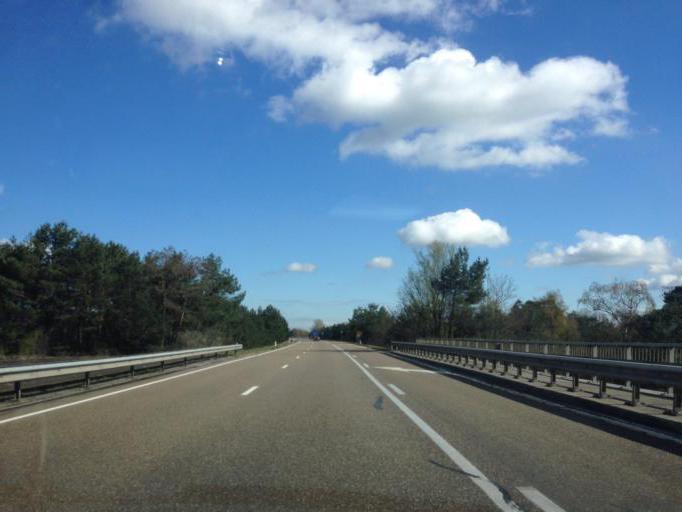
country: BE
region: Flanders
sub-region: Provincie Limburg
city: Overpelt
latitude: 51.2320
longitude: 5.4072
